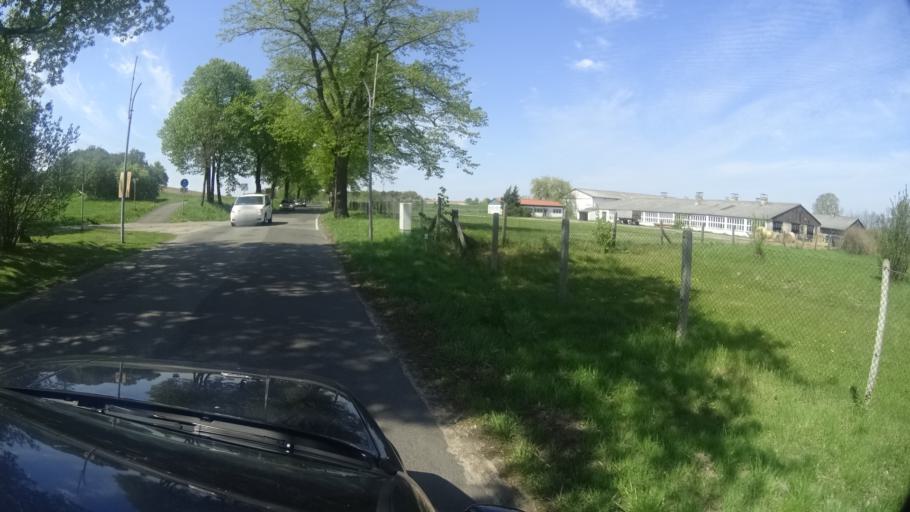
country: DE
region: Brandenburg
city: Rhinow
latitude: 52.7547
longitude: 12.3683
